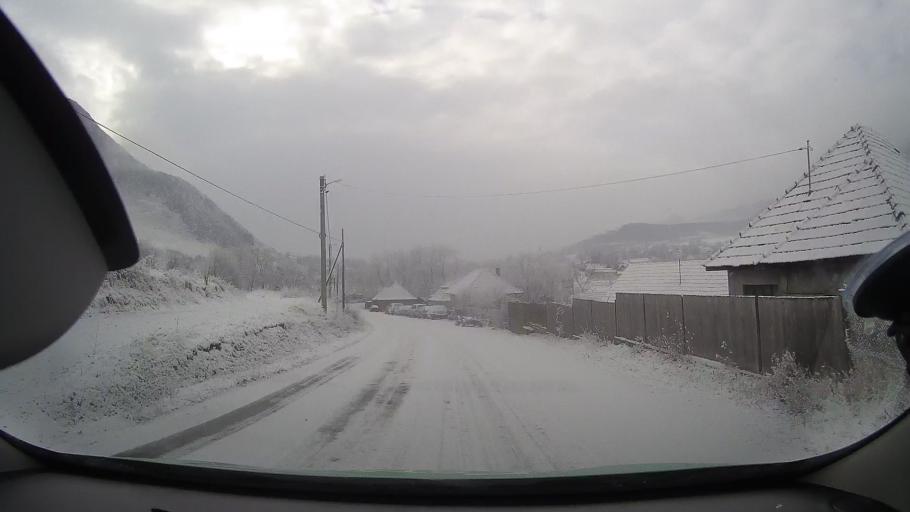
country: RO
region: Alba
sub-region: Comuna Rimetea
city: Rimetea
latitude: 46.4602
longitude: 23.5716
